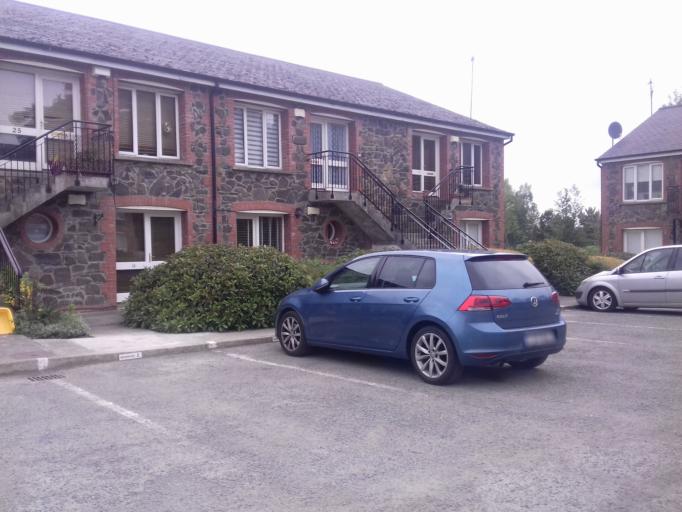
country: IE
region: Leinster
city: Donabate
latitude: 53.4934
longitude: -6.1752
